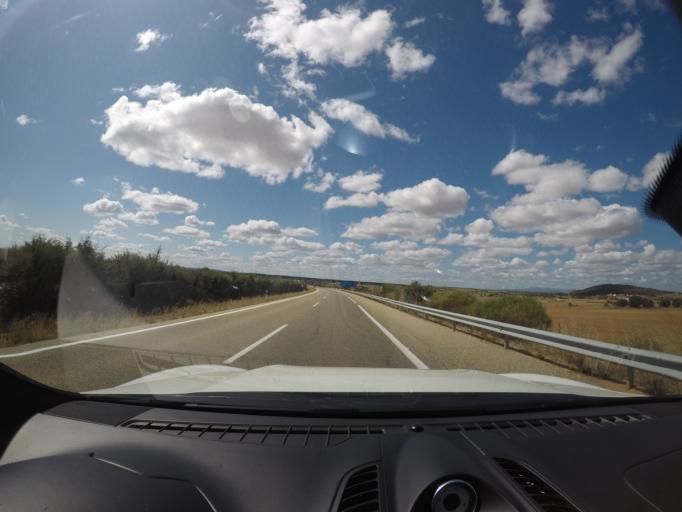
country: ES
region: Castille and Leon
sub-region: Provincia de Zamora
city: Quiruelas de Vidriales
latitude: 42.0268
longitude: -5.8348
